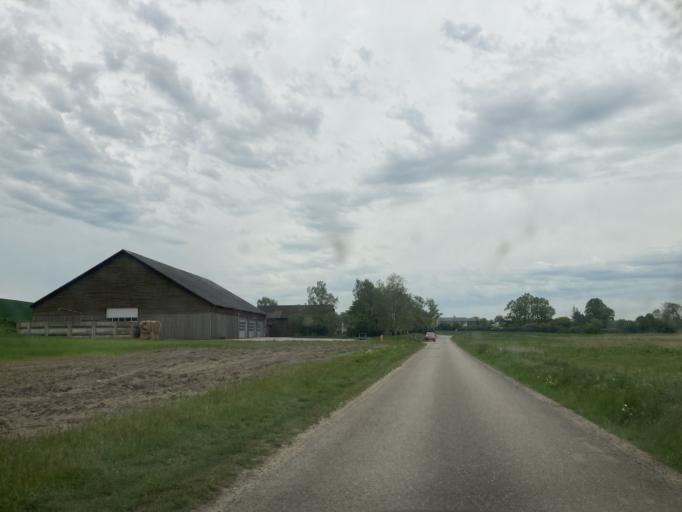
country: DK
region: Zealand
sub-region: Roskilde Kommune
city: Svogerslev
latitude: 55.6795
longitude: 11.9990
